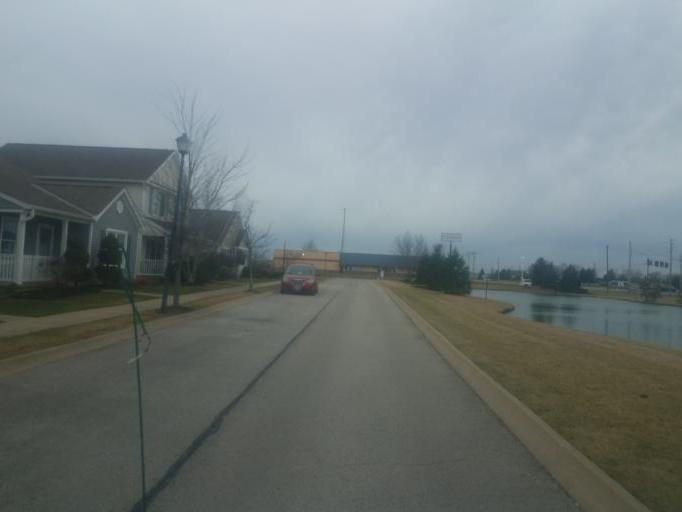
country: US
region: Ohio
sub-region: Marion County
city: Marion
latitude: 40.5809
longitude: -83.0684
